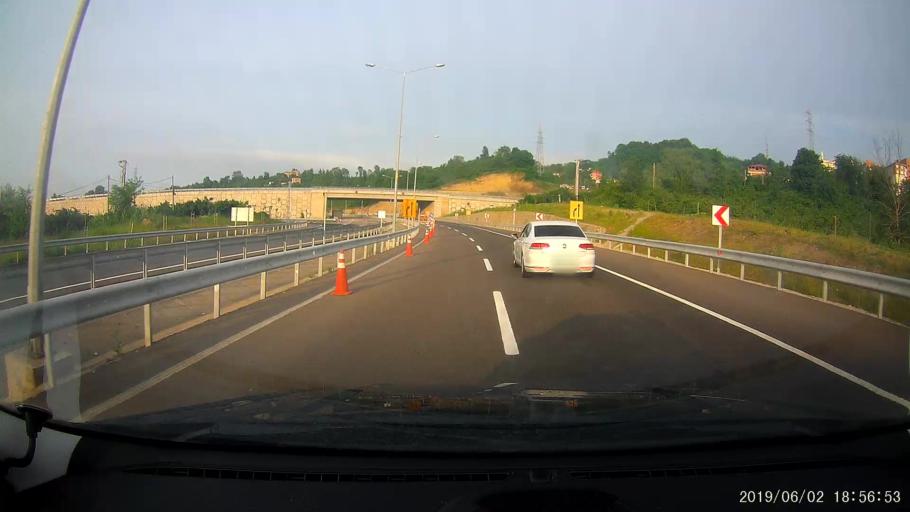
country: TR
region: Ordu
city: Ordu
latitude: 40.9535
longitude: 37.9008
